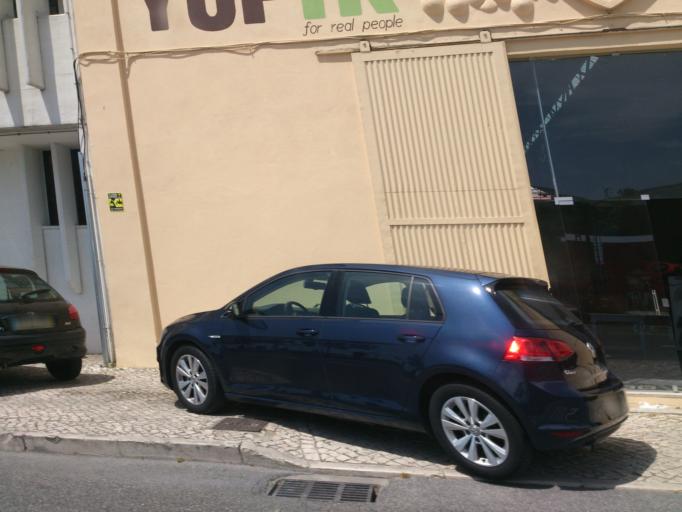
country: PT
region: Lisbon
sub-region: Loures
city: Moscavide
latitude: 38.7409
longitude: -9.1013
